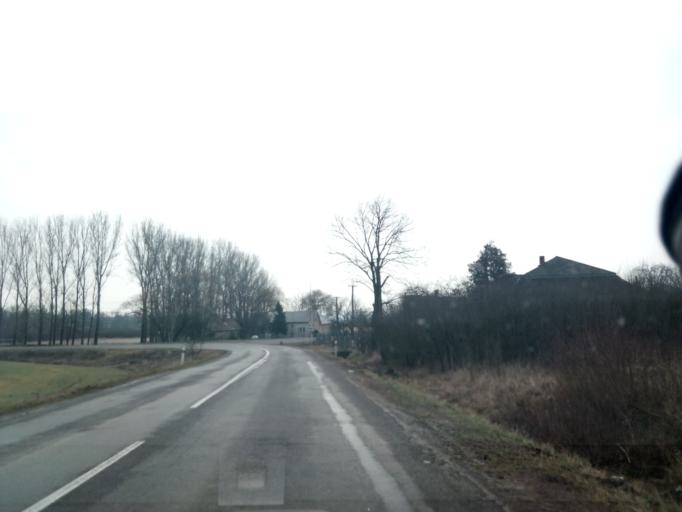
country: SK
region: Kosicky
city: Secovce
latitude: 48.6077
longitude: 21.6186
